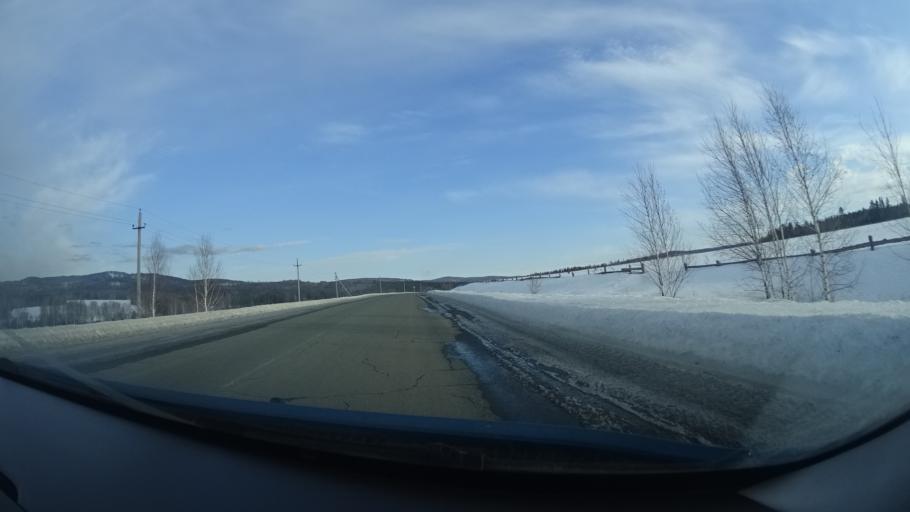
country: RU
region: Bashkortostan
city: Lomovka
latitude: 53.7204
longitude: 58.2558
